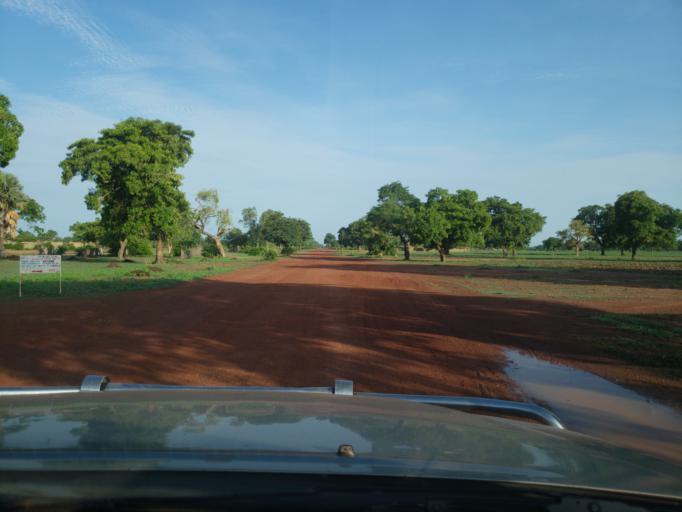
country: ML
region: Sikasso
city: Koutiala
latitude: 12.4163
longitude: -5.5708
